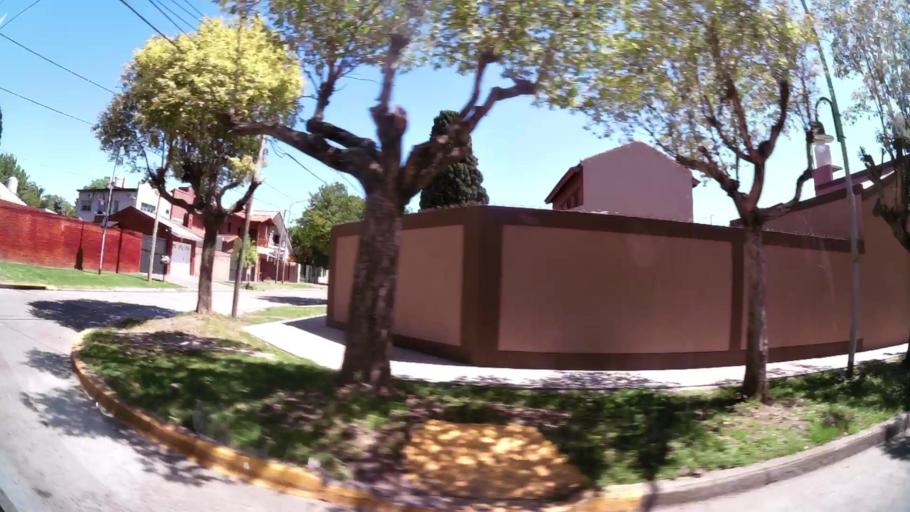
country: AR
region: Buenos Aires
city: Hurlingham
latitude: -34.5014
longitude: -58.6380
